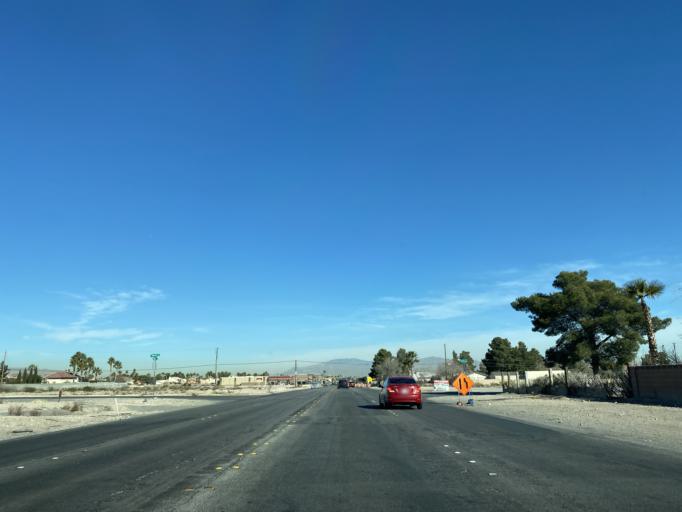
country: US
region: Nevada
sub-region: Clark County
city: Spring Valley
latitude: 36.0813
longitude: -115.2250
